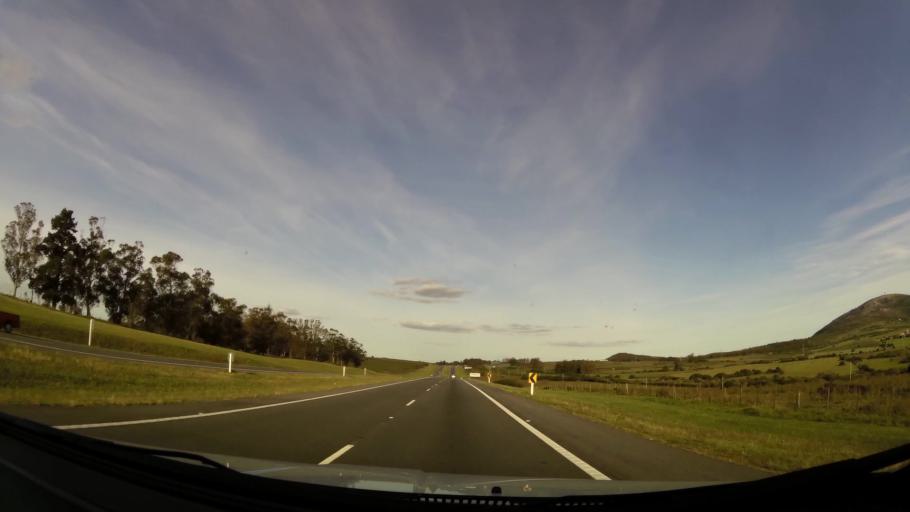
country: UY
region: Maldonado
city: Pan de Azucar
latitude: -34.7878
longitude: -55.2873
